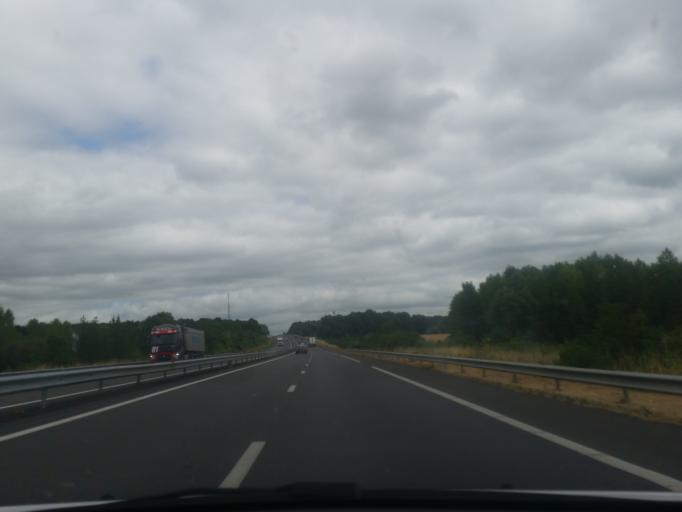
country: FR
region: Pays de la Loire
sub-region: Departement de Maine-et-Loire
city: Seiches-sur-le-Loir
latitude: 47.5973
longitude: -0.3128
